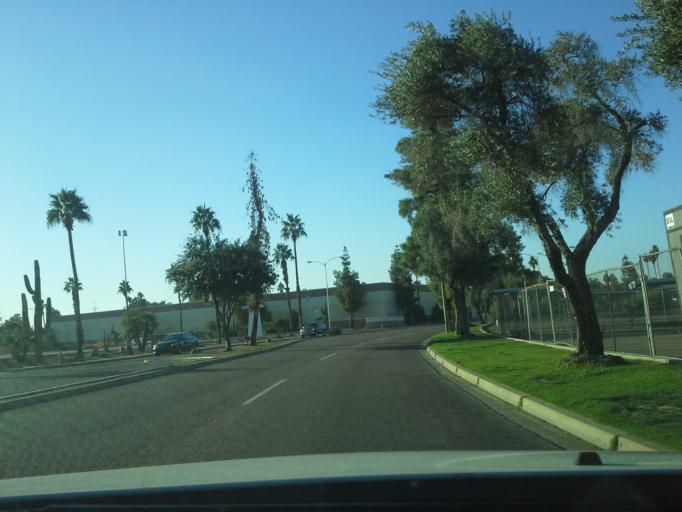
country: US
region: Arizona
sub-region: Maricopa County
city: Glendale
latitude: 33.5717
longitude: -112.1226
